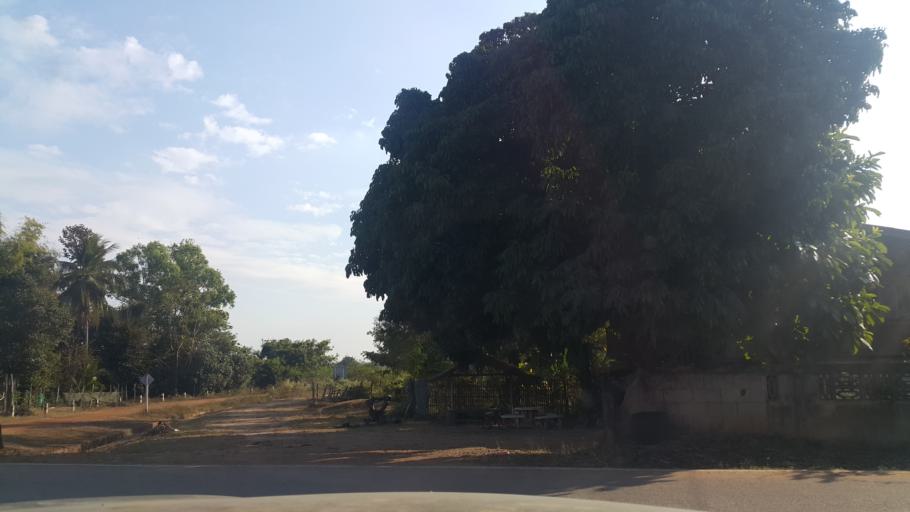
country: TH
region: Lampang
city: Ko Kha
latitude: 18.2292
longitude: 99.3539
